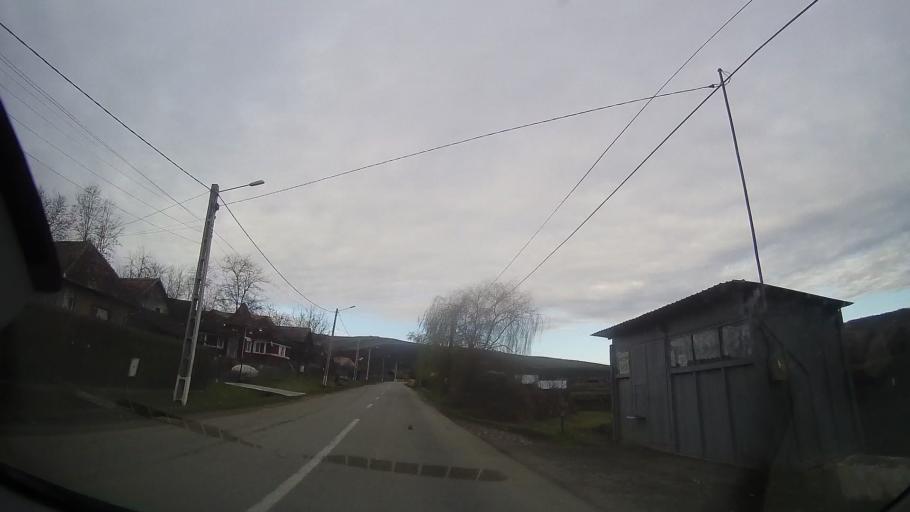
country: RO
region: Cluj
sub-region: Comuna Camarasu
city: Camarasu
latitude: 46.8171
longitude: 24.1379
